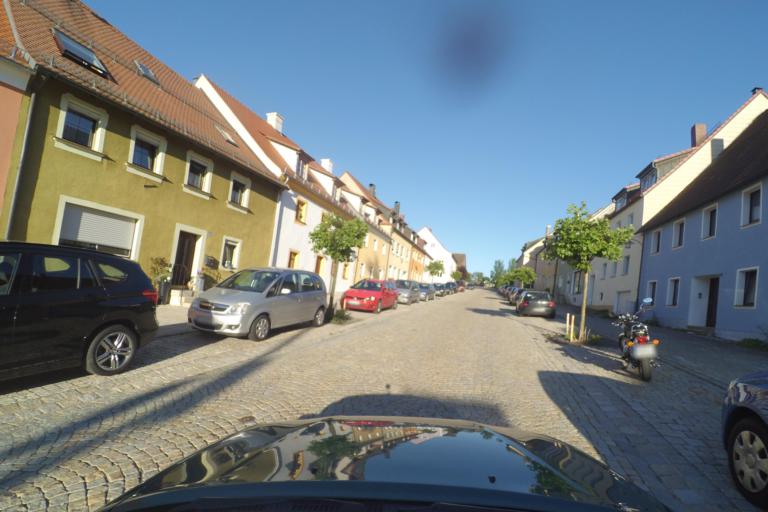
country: DE
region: Bavaria
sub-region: Upper Palatinate
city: Kastl
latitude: 49.8629
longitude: 11.9513
